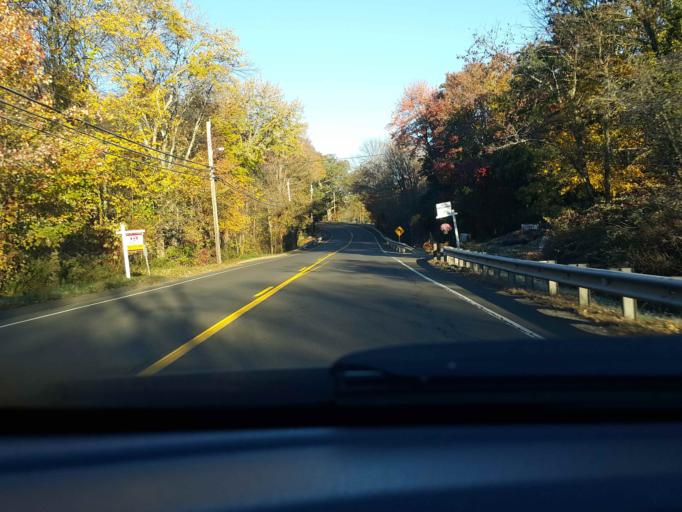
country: US
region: Connecticut
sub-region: New Haven County
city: Seymour
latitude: 41.3908
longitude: -73.0368
